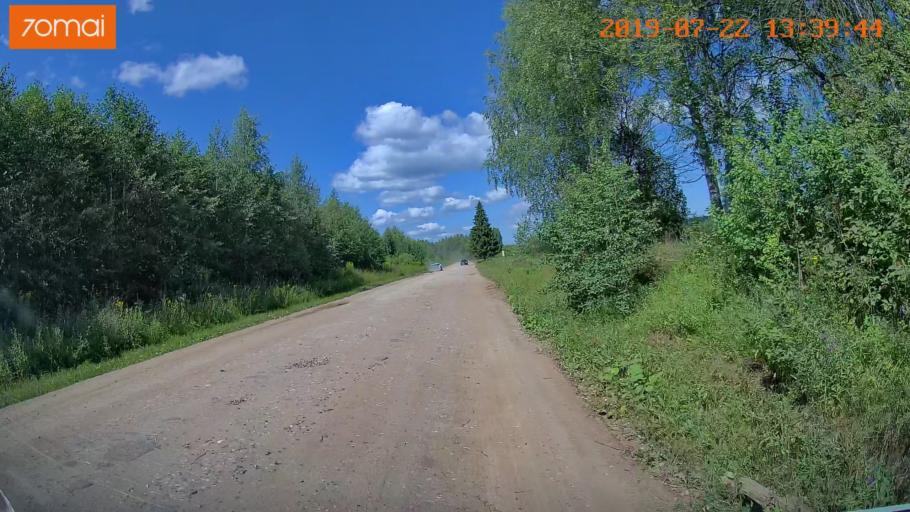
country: RU
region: Ivanovo
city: Novo-Talitsy
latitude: 57.0737
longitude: 40.8816
